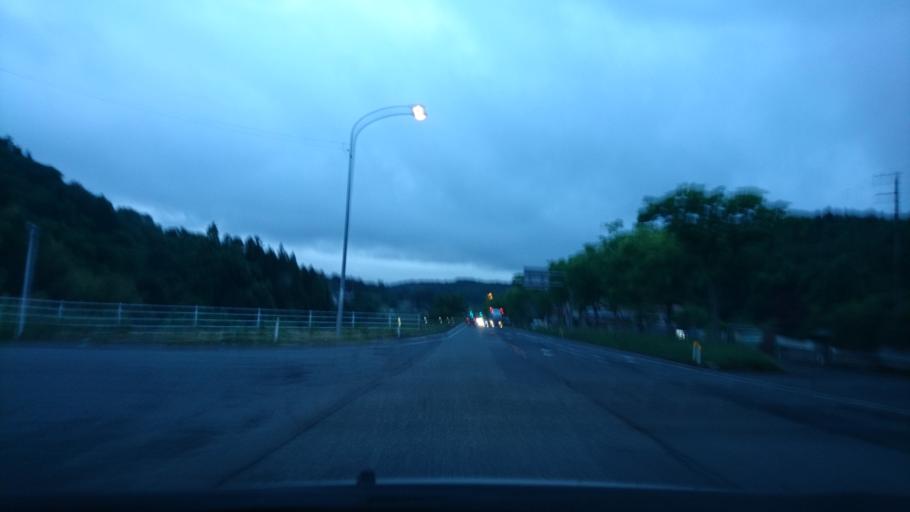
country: JP
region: Iwate
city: Ichinoseki
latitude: 38.8364
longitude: 141.0880
